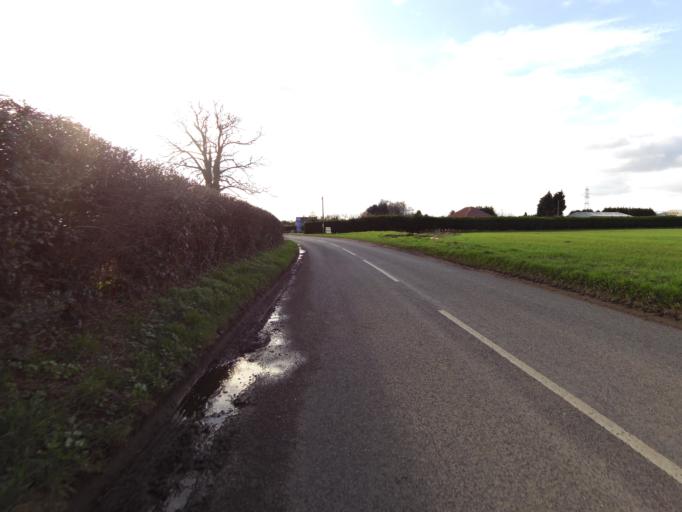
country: GB
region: England
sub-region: East Riding of Yorkshire
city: Snaith
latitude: 53.7055
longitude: -1.0327
